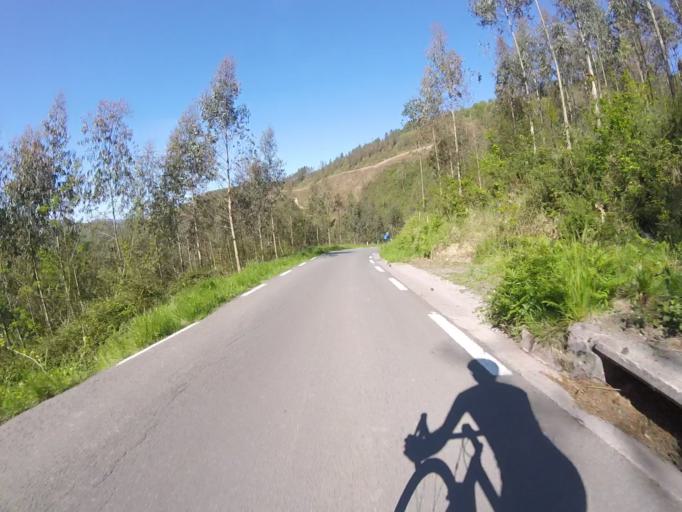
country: ES
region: Basque Country
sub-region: Provincia de Guipuzcoa
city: Errezil
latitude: 43.1883
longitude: -2.1944
